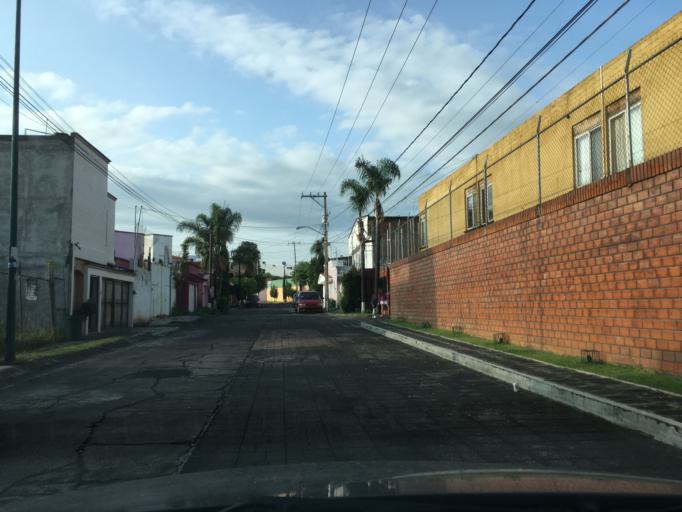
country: MX
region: Michoacan
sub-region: Morelia
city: Morelos
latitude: 19.6796
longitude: -101.2270
